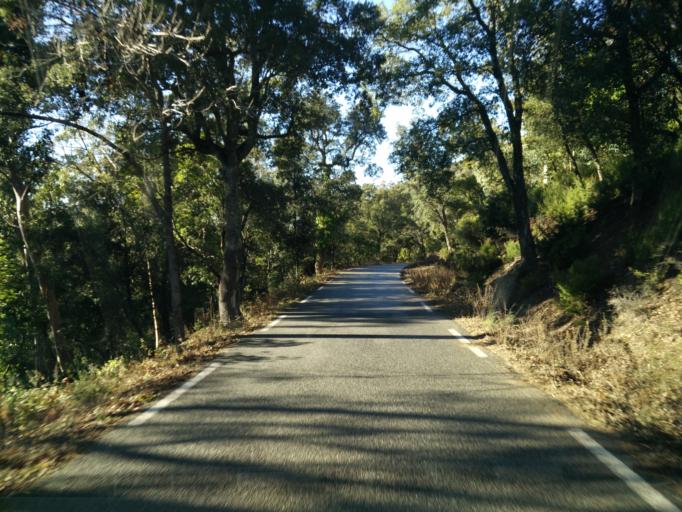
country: FR
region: Provence-Alpes-Cote d'Azur
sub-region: Departement du Var
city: Collobrieres
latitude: 43.2446
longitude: 6.3711
